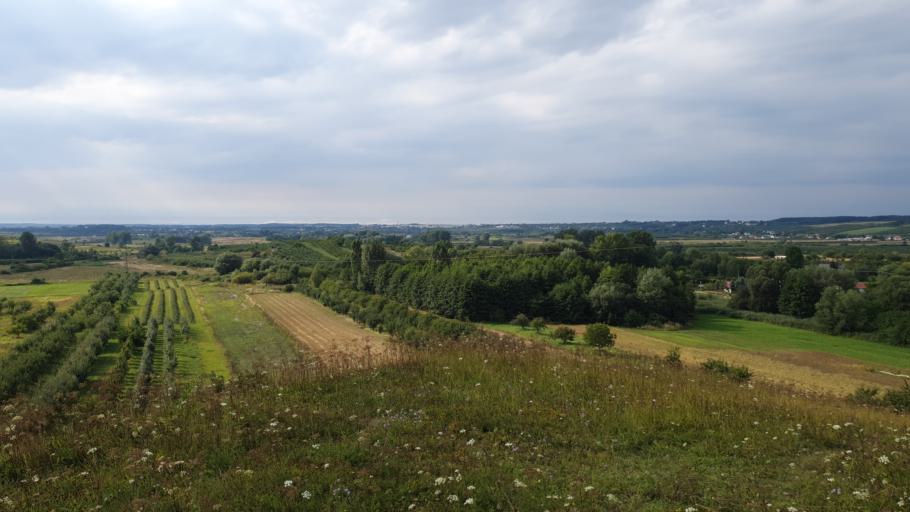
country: PL
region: Swietokrzyskie
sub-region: Powiat buski
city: Busko-Zdroj
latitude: 50.4433
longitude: 20.7850
